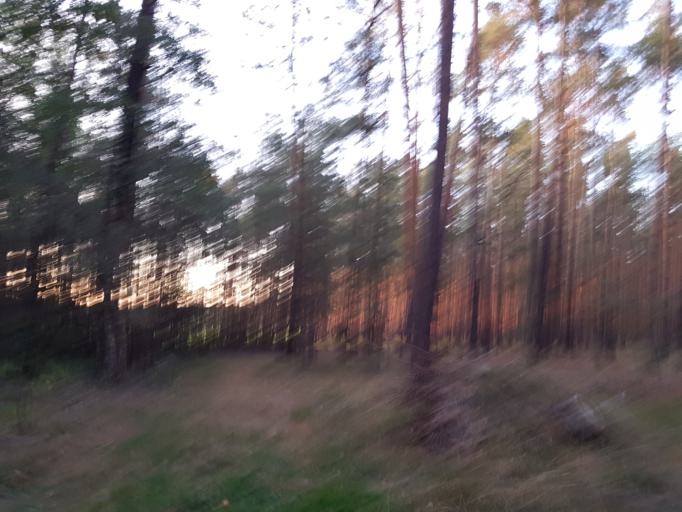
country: DE
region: Brandenburg
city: Trobitz
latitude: 51.5563
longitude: 13.4284
